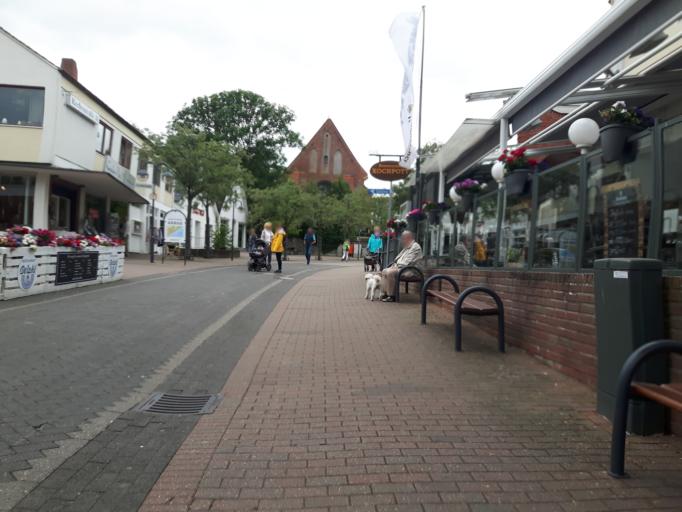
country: DE
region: Schleswig-Holstein
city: Gromitz
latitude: 54.1497
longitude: 10.9589
